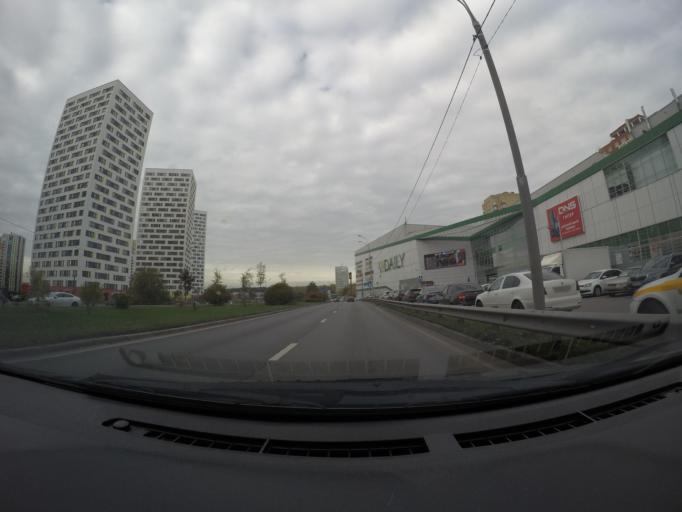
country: RU
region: Moskovskaya
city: Mytishchi
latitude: 55.9208
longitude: 37.7188
